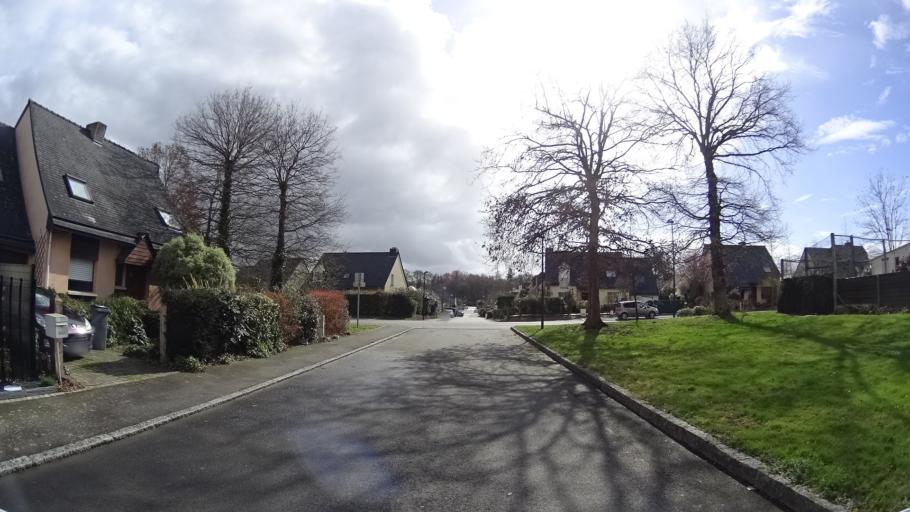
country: FR
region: Brittany
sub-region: Departement d'Ille-et-Vilaine
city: Saint-Gilles
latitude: 48.1523
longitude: -1.8355
